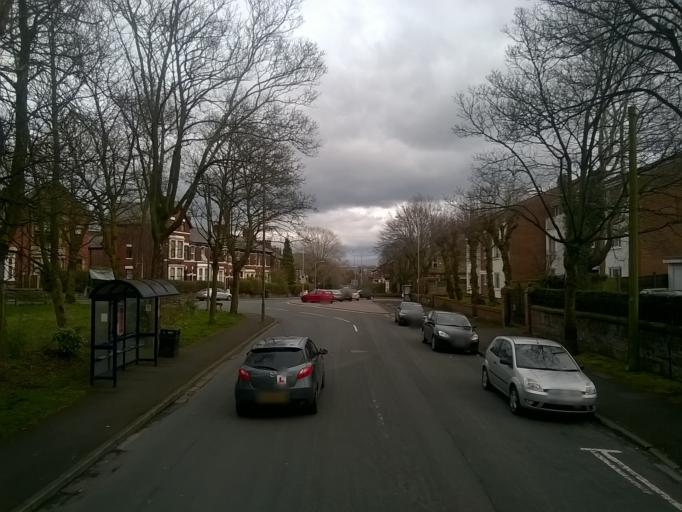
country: GB
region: England
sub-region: Lancashire
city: Preston
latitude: 53.7648
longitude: -2.7314
